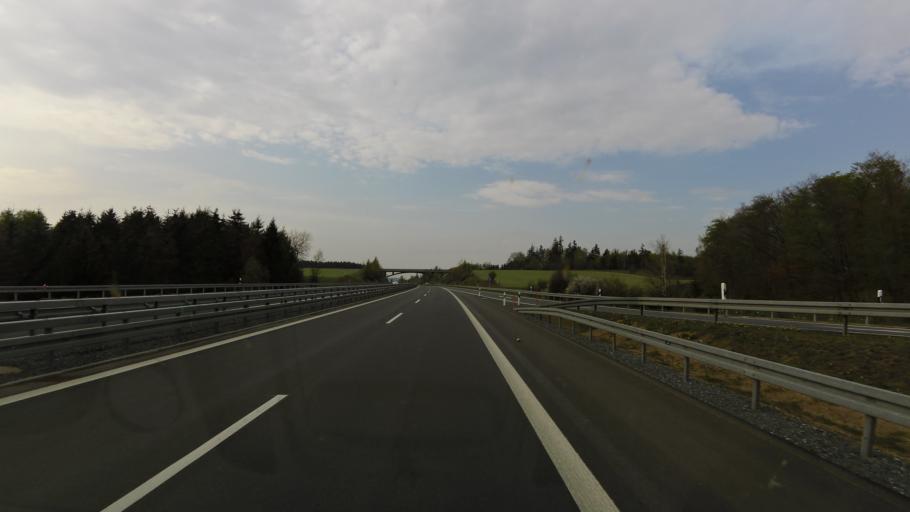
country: DE
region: Bavaria
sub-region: Upper Franconia
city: Gattendorf
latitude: 50.3259
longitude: 12.0229
